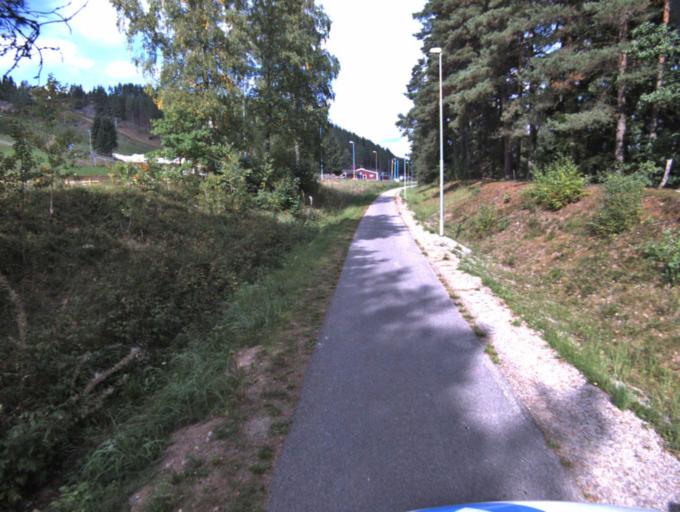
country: SE
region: Vaestra Goetaland
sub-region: Ulricehamns Kommun
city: Ulricehamn
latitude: 57.8182
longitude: 13.4121
